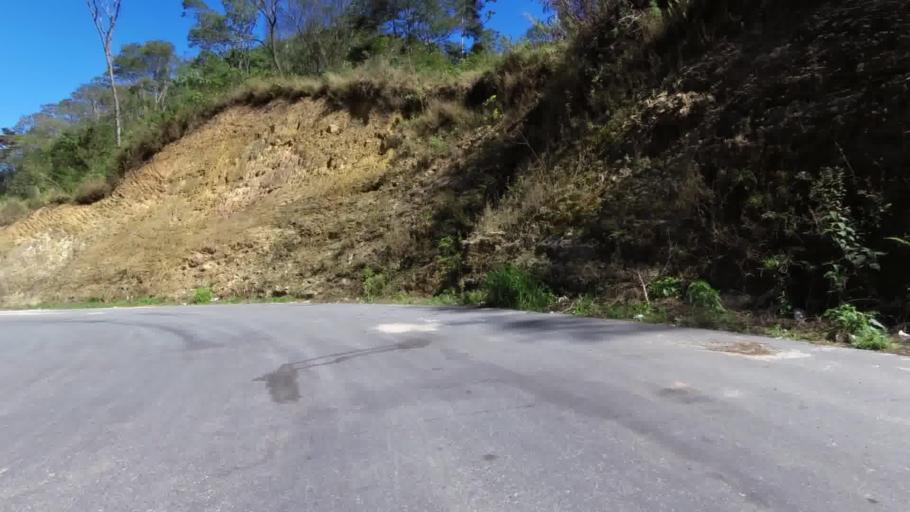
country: BR
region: Espirito Santo
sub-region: Vargem Alta
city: Vargem Alta
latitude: -20.6792
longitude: -41.0256
